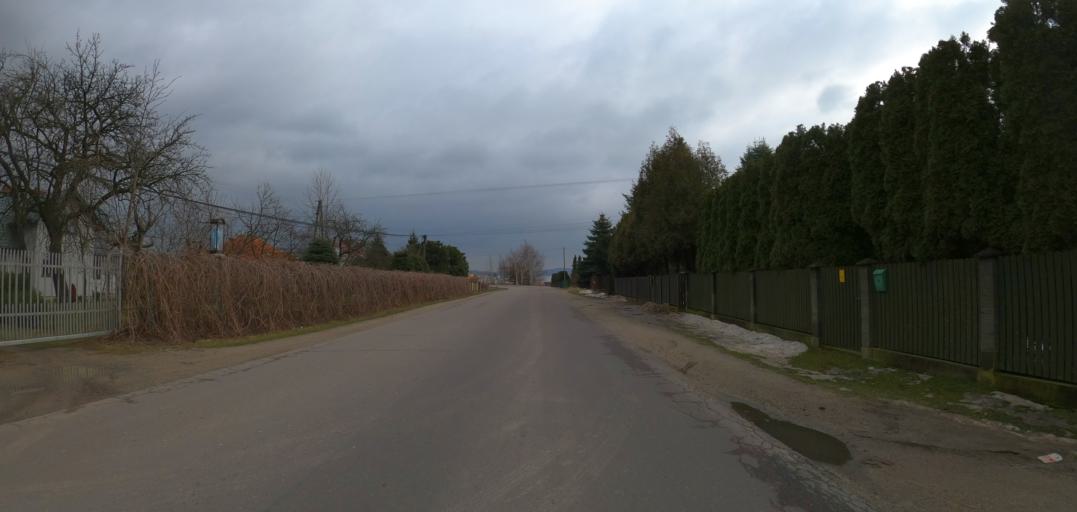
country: PL
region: Subcarpathian Voivodeship
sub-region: Powiat debicki
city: Pilzno
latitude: 49.9884
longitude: 21.3137
